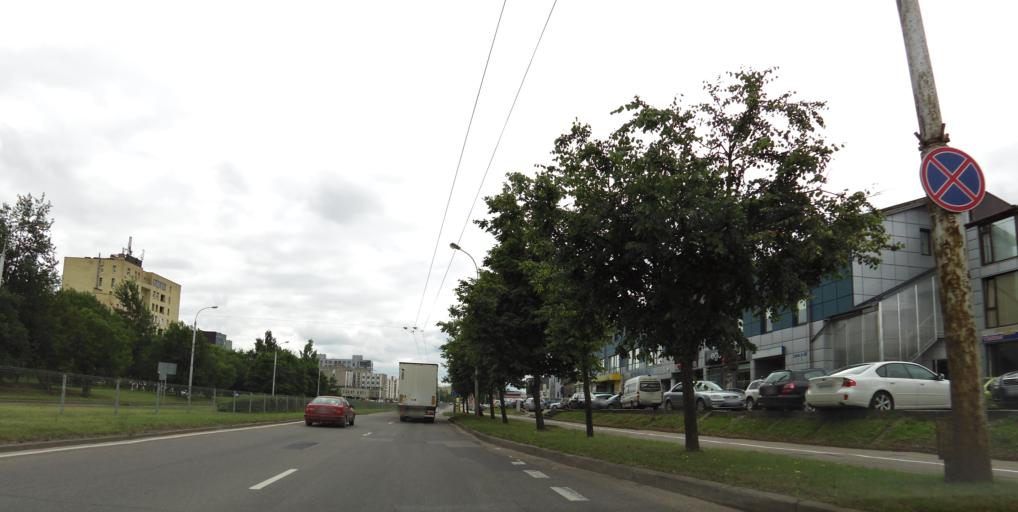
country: LT
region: Vilnius County
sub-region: Vilnius
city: Fabijoniskes
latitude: 54.7255
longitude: 25.2333
